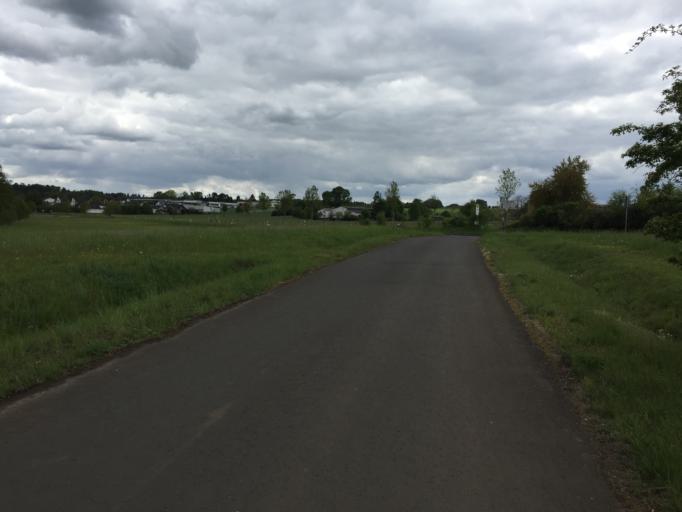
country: DE
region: Hesse
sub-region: Regierungsbezirk Giessen
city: Grunberg
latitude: 50.5664
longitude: 8.8981
